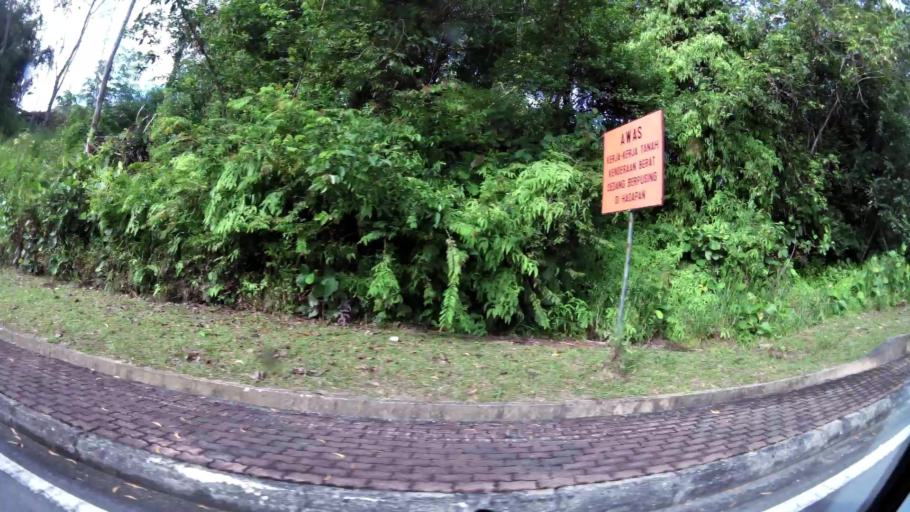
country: BN
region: Brunei and Muara
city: Bandar Seri Begawan
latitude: 4.8864
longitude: 114.9517
